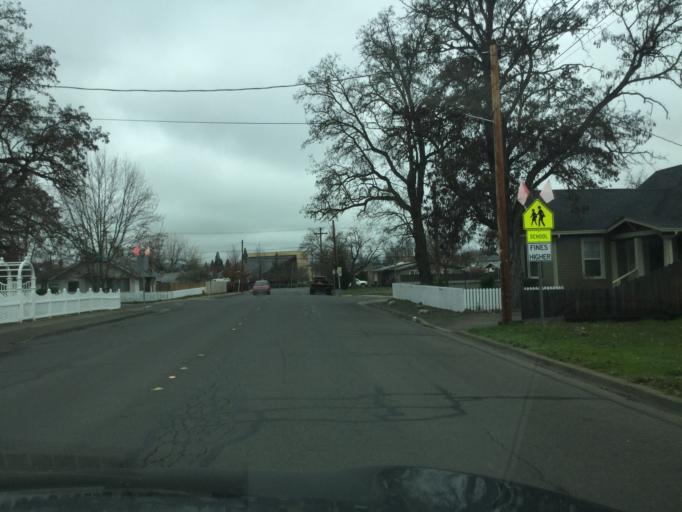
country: US
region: Oregon
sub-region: Jackson County
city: Central Point
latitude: 42.3781
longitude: -122.9182
